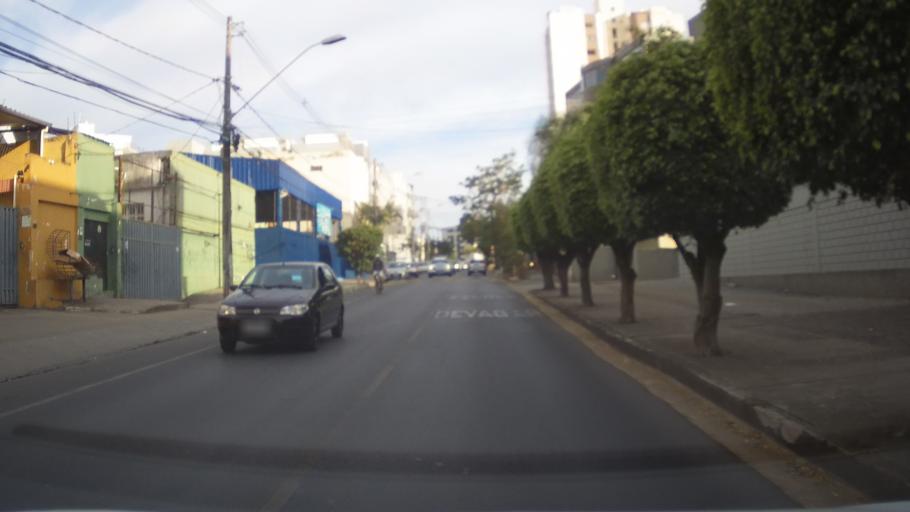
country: BR
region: Minas Gerais
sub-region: Belo Horizonte
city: Belo Horizonte
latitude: -19.8734
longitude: -43.9888
